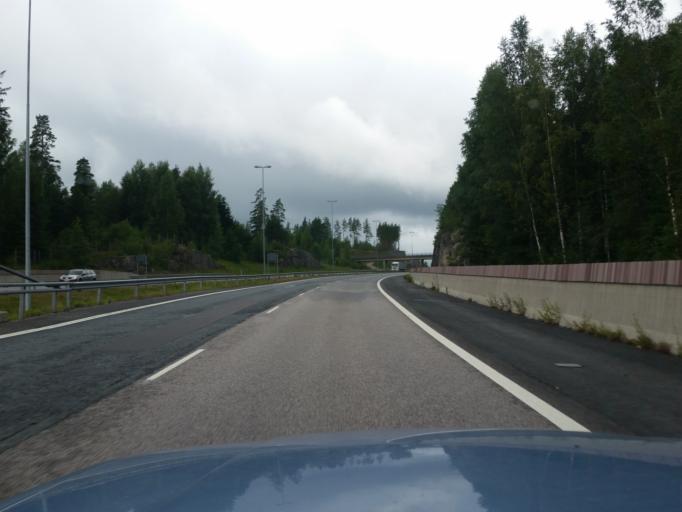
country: FI
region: Uusimaa
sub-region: Helsinki
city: Vihti
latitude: 60.3001
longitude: 24.2312
